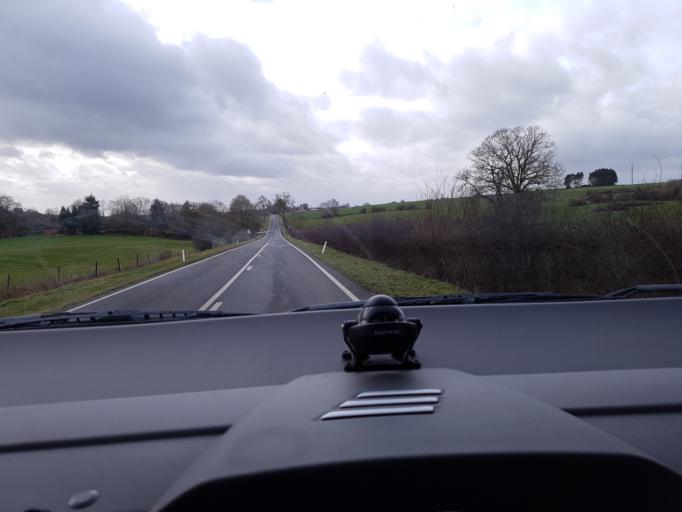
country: BE
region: Wallonia
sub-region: Province du Hainaut
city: Beaumont
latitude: 50.2288
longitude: 4.3007
